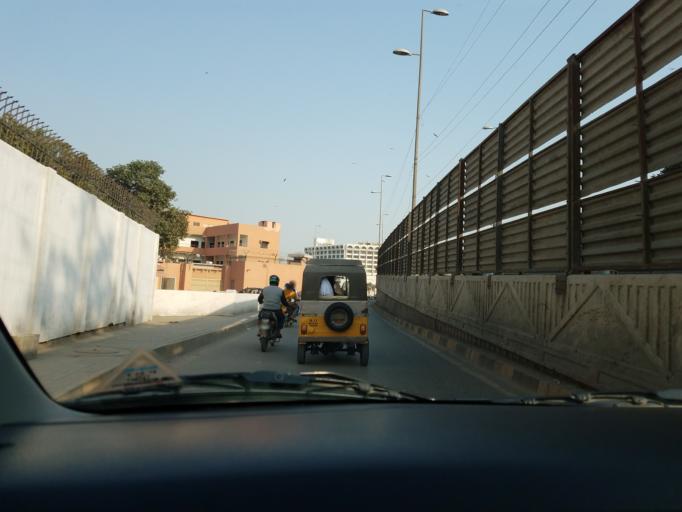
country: PK
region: Sindh
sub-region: Karachi District
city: Karachi
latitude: 24.8561
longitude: 67.0367
